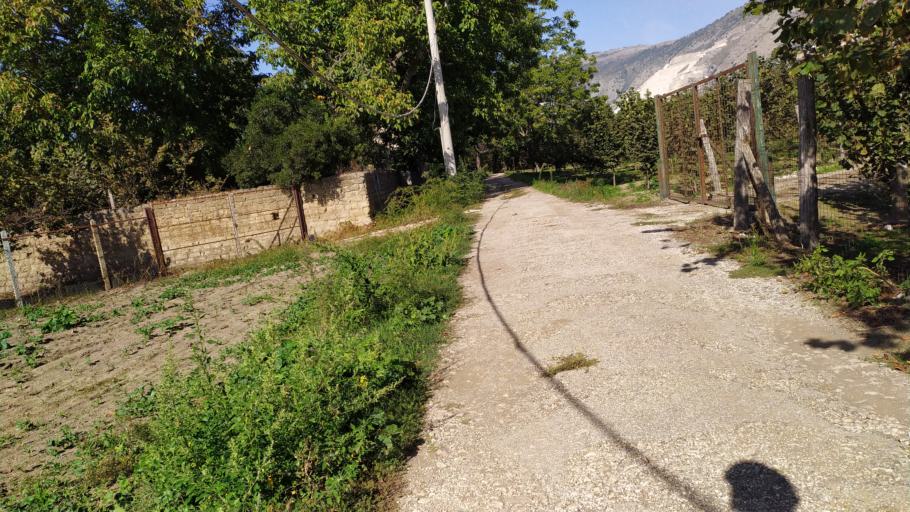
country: IT
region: Campania
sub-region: Provincia di Napoli
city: Camposano
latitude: 40.9630
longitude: 14.5183
